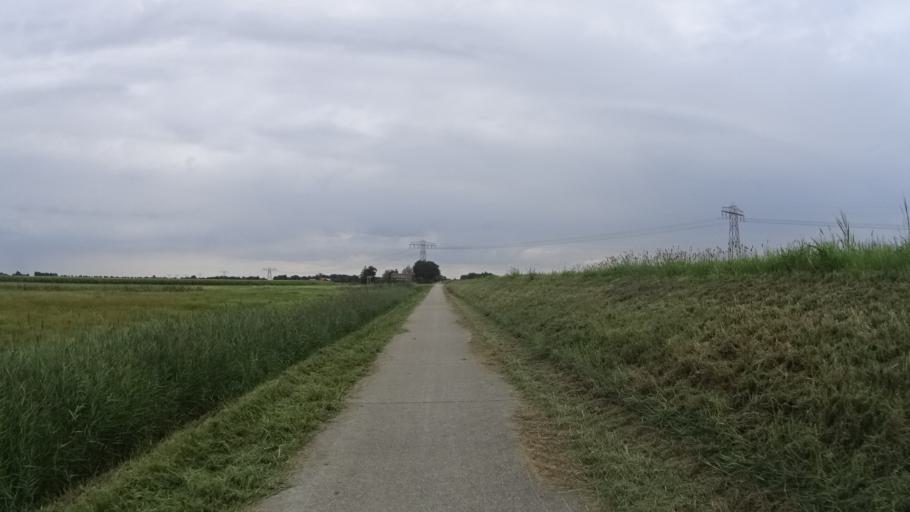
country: NL
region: Groningen
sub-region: Gemeente Hoogezand-Sappemeer
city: Hoogezand
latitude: 53.2355
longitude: 6.6962
